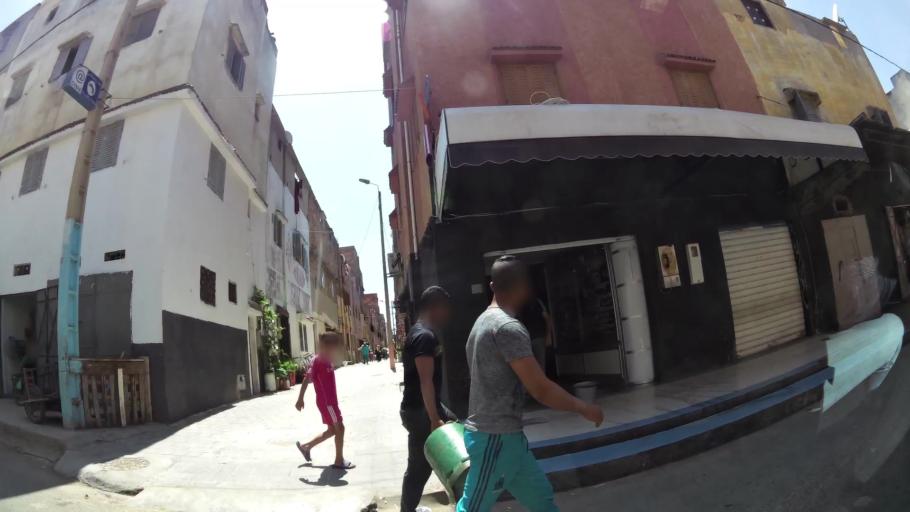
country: MA
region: Gharb-Chrarda-Beni Hssen
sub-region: Kenitra Province
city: Kenitra
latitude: 34.2576
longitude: -6.5536
